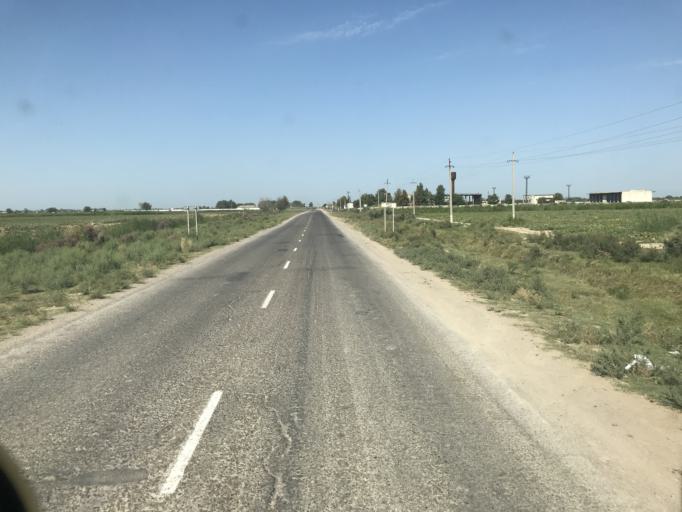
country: KZ
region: Ongtustik Qazaqstan
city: Myrzakent
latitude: 40.6855
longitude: 68.5675
